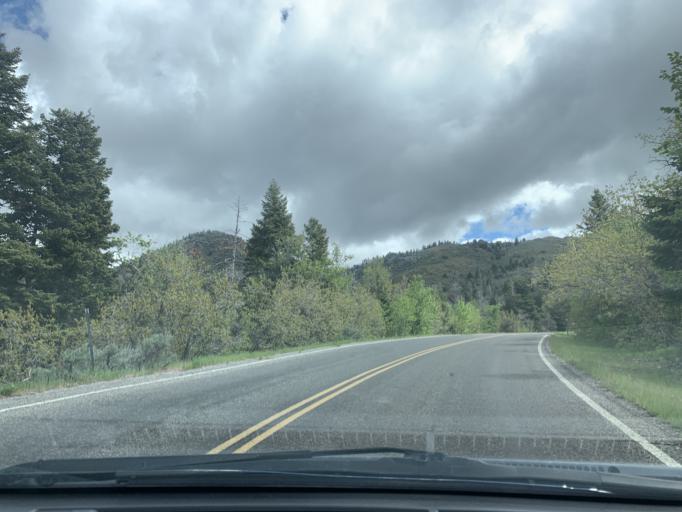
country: US
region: Utah
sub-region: Juab County
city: Nephi
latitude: 39.7860
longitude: -111.6904
